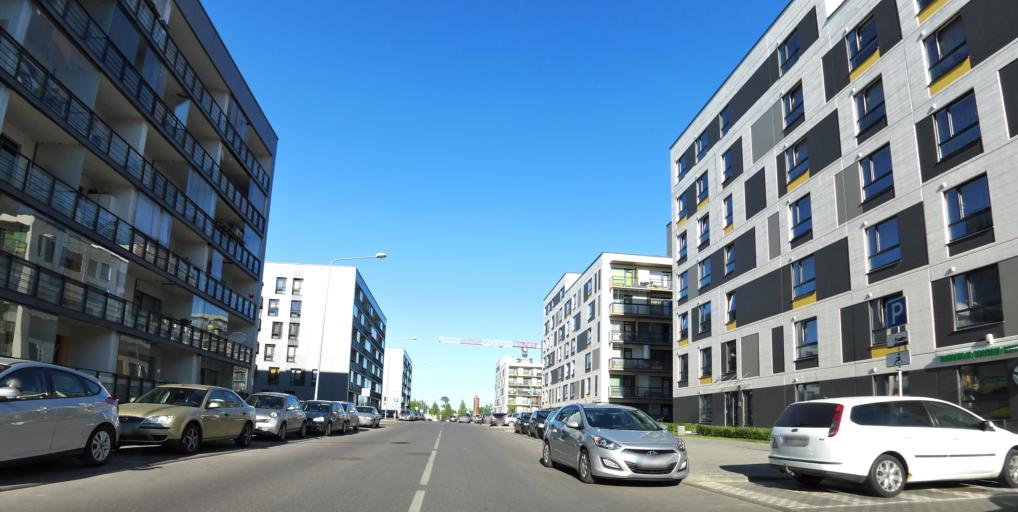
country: LT
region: Vilnius County
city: Pilaite
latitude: 54.7116
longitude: 25.1843
